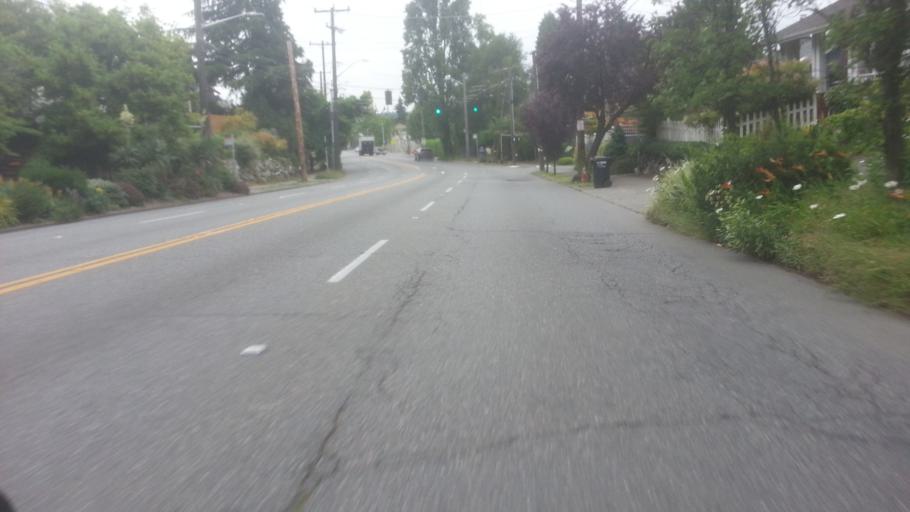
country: US
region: Washington
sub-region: King County
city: Seattle
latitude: 47.6373
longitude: -122.3015
